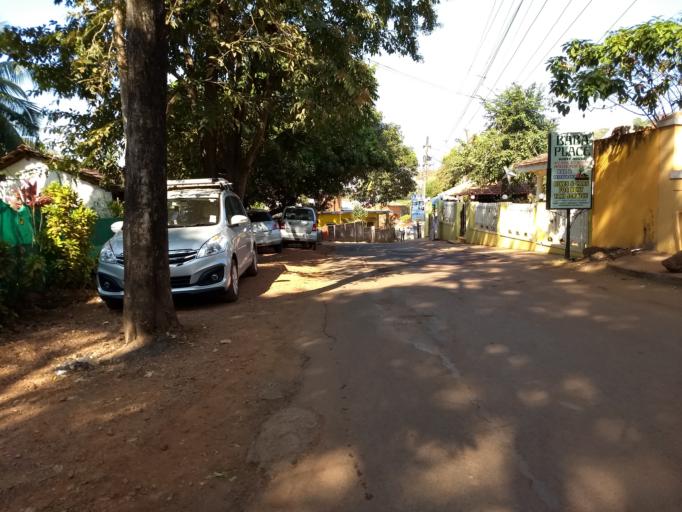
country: IN
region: Goa
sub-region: North Goa
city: Vagator
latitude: 15.6017
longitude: 73.7379
